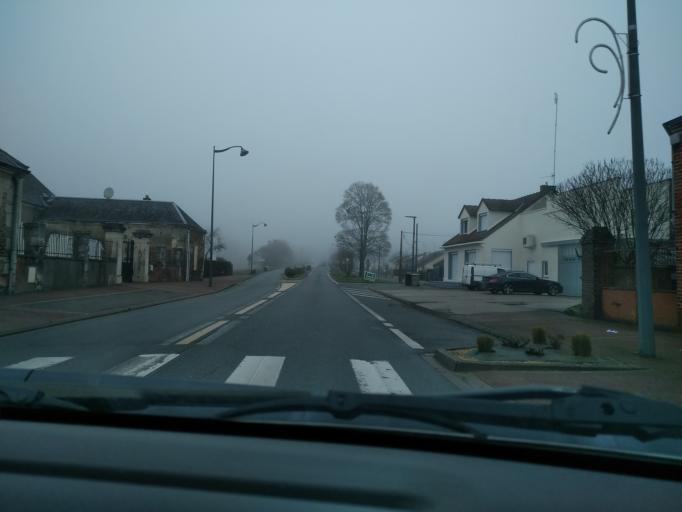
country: FR
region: Centre
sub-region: Departement d'Eure-et-Loir
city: Marboue
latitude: 48.1154
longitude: 1.3303
